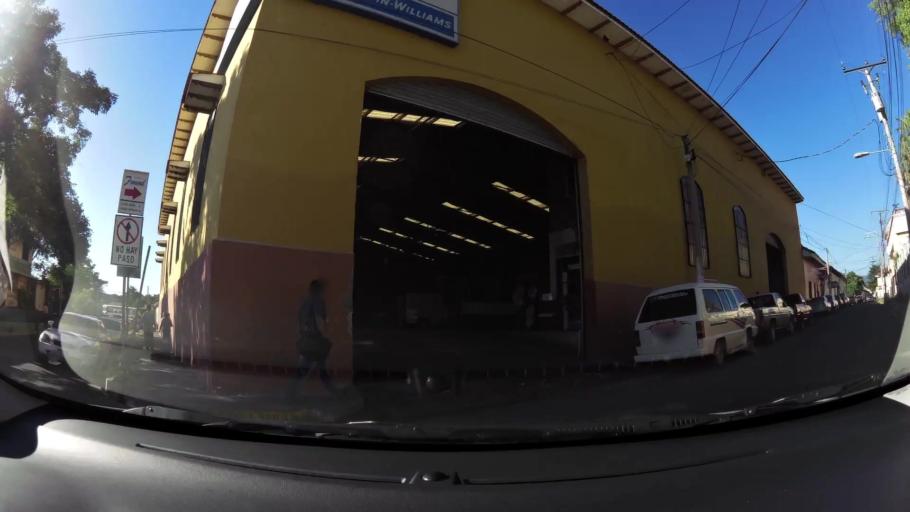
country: SV
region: San Miguel
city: San Miguel
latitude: 13.4821
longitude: -88.1738
